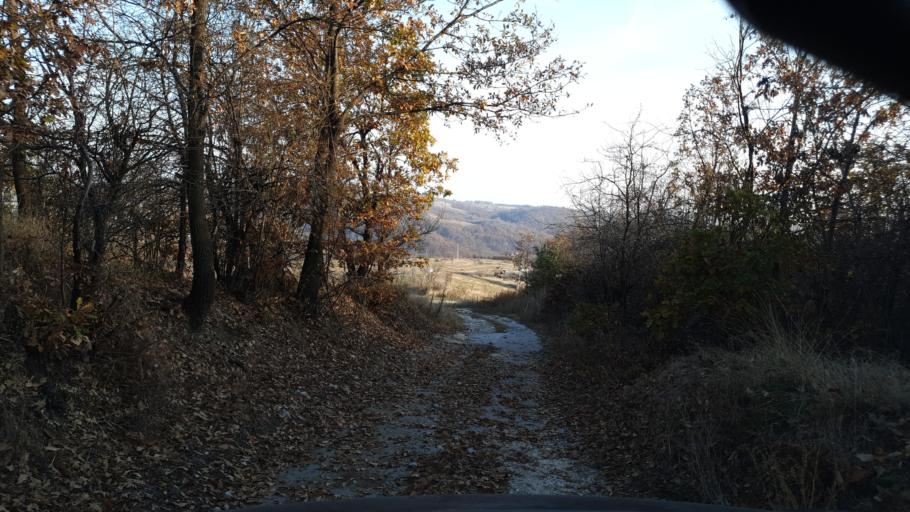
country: RS
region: Central Serbia
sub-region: Borski Okrug
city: Bor
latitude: 44.0516
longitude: 22.0887
